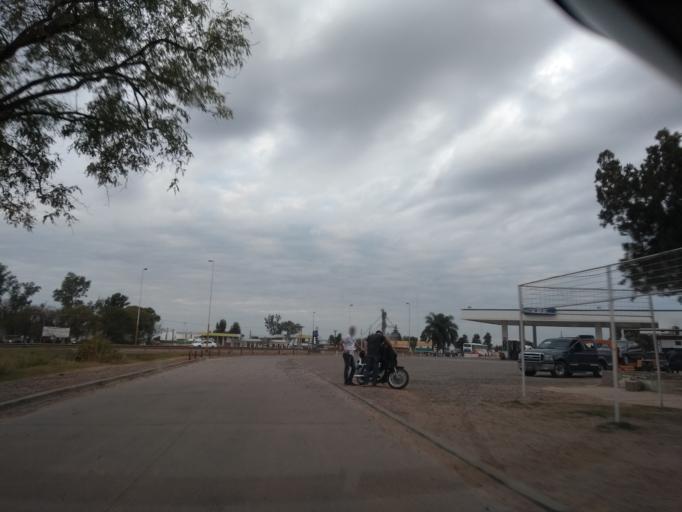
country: AR
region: Chaco
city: Presidencia Roque Saenz Pena
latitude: -26.8136
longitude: -60.4175
